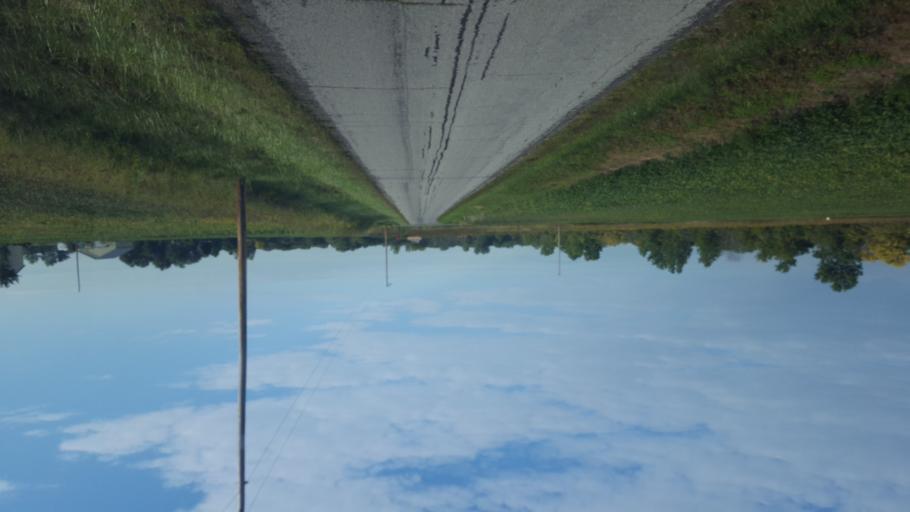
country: US
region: Ohio
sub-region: Morrow County
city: Mount Gilead
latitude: 40.6450
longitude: -82.8900
